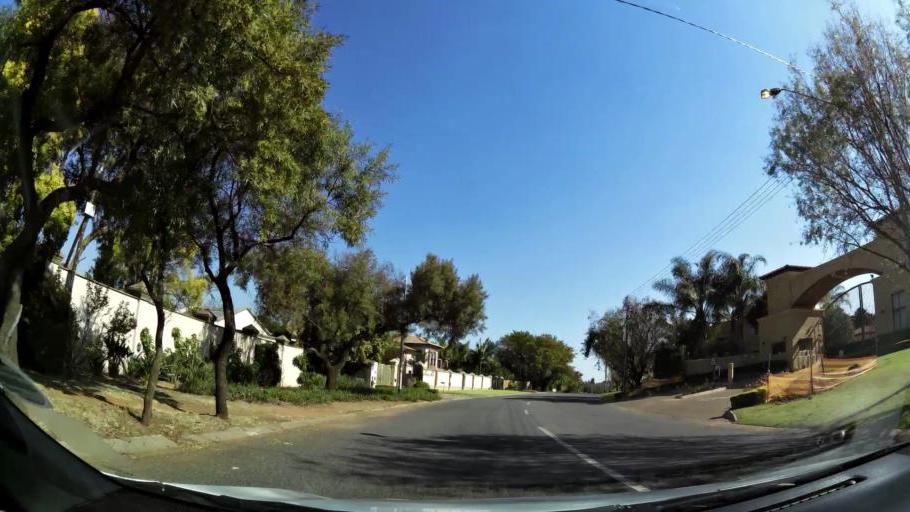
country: ZA
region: Gauteng
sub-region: City of Tshwane Metropolitan Municipality
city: Pretoria
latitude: -25.7572
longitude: 28.2722
